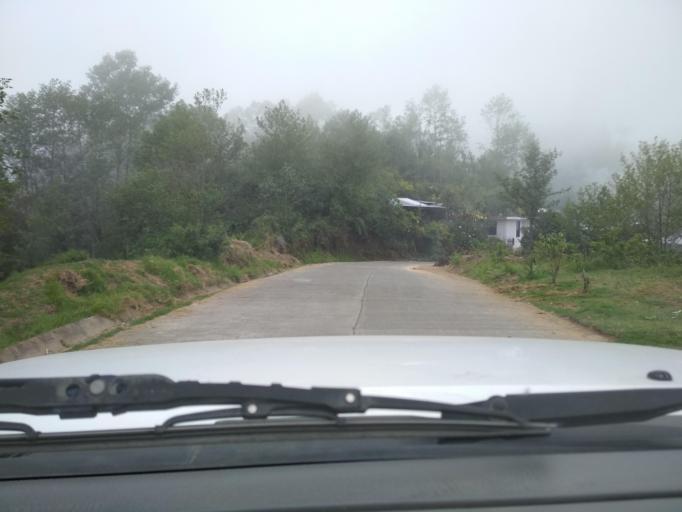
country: MX
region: Veracruz
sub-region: La Perla
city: Chilapa
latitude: 18.9729
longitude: -97.1598
